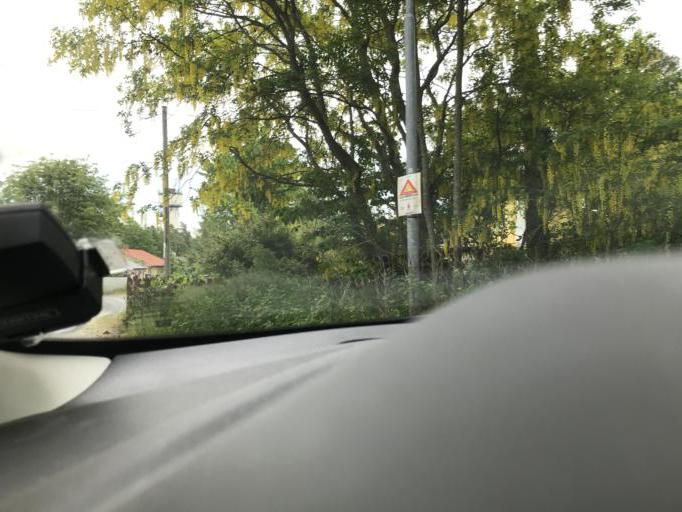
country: SE
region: Stockholm
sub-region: Botkyrka Kommun
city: Tumba
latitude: 59.1978
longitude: 17.8154
